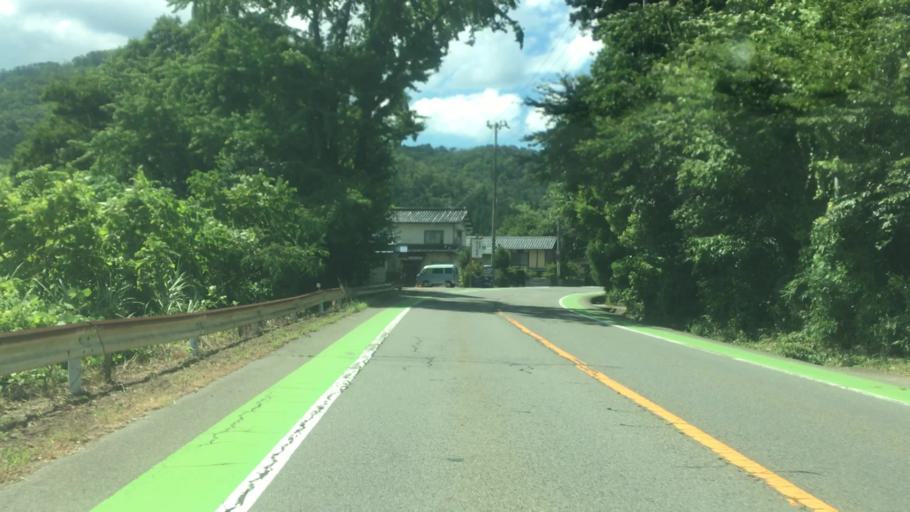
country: JP
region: Hyogo
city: Toyooka
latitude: 35.4767
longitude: 134.7104
